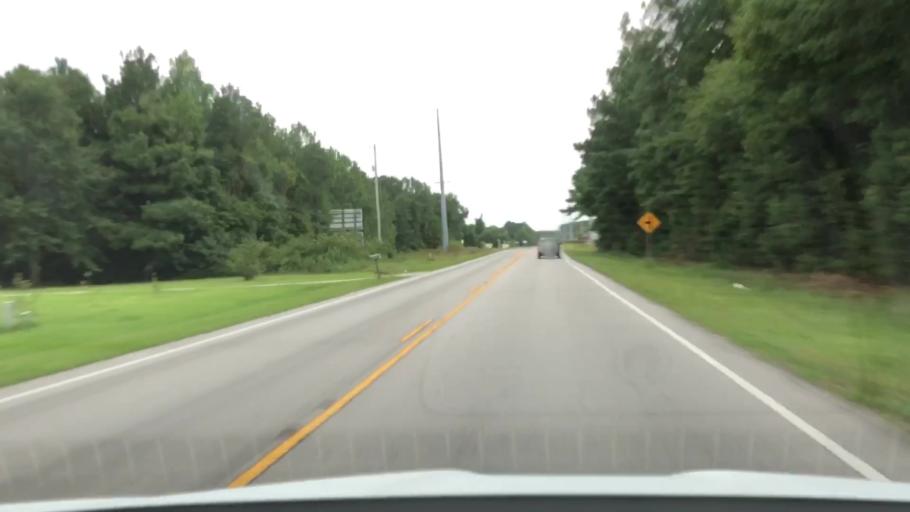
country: US
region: North Carolina
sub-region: Carteret County
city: Cape Carteret
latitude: 34.7563
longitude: -77.0938
